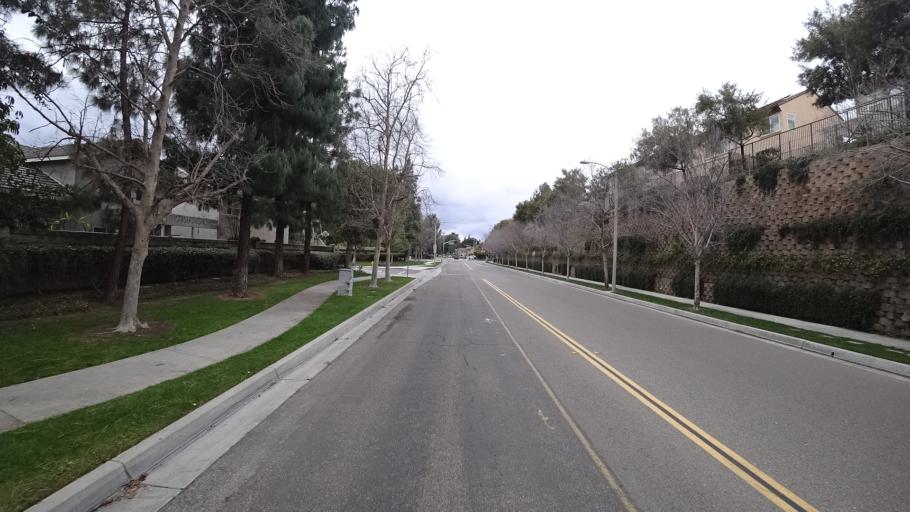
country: US
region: California
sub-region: Orange County
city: Yorba Linda
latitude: 33.8701
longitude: -117.8248
